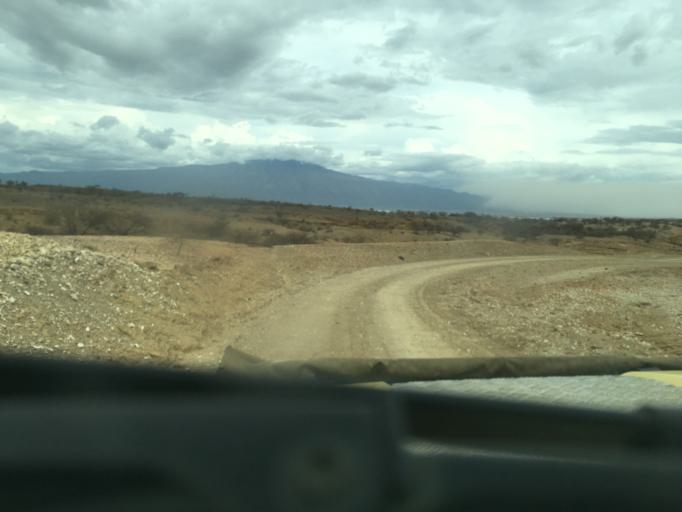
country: KE
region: Kajiado
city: Magadi
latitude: -2.4935
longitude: 35.8701
